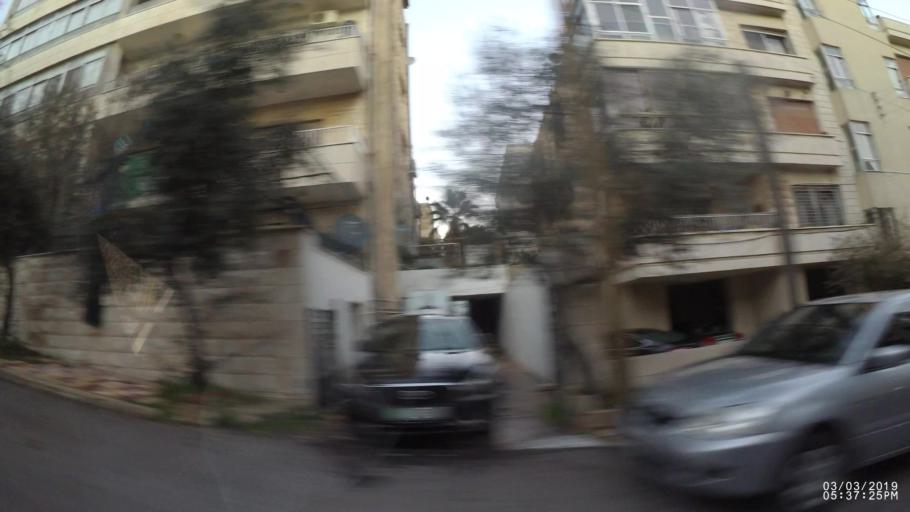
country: JO
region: Amman
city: Al Jubayhah
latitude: 31.9916
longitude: 35.8835
